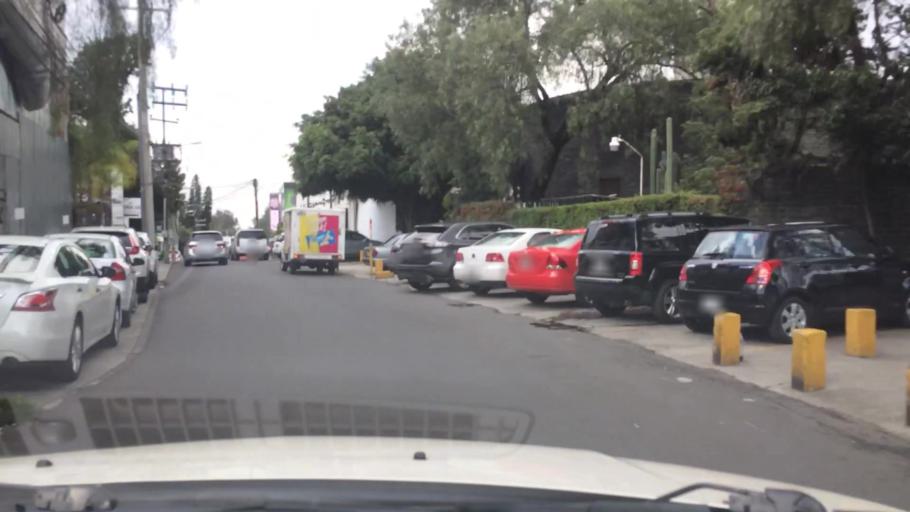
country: MX
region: Mexico City
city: Magdalena Contreras
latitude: 19.3157
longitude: -99.2125
